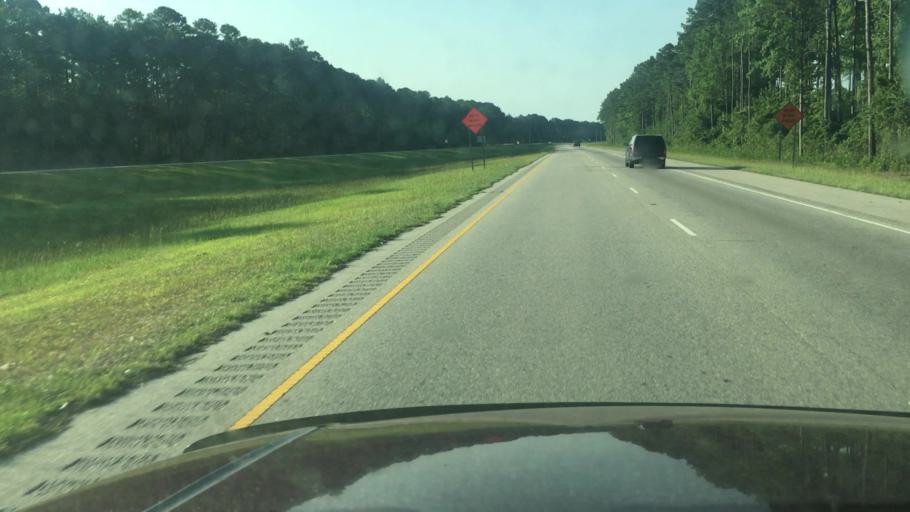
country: US
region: North Carolina
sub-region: Cumberland County
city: Vander
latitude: 34.9670
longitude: -78.8499
